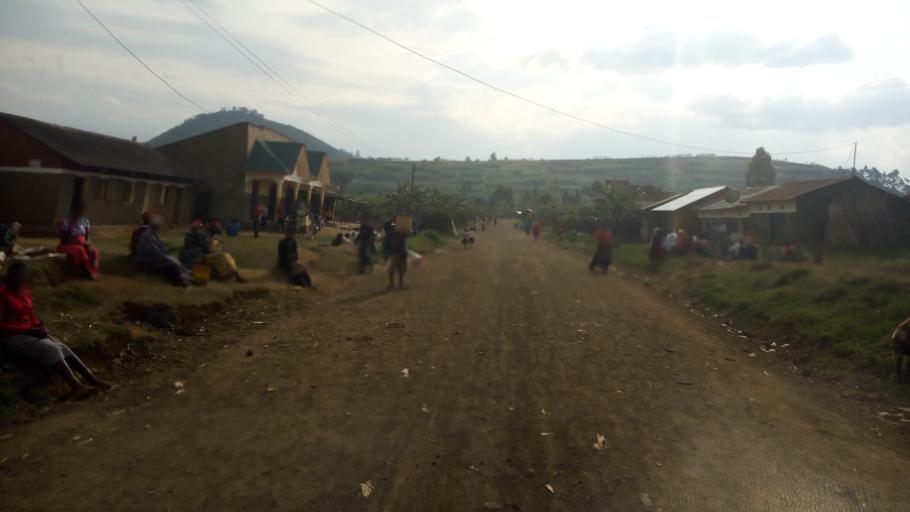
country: UG
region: Western Region
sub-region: Kisoro District
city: Kisoro
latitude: -1.3026
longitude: 29.7061
